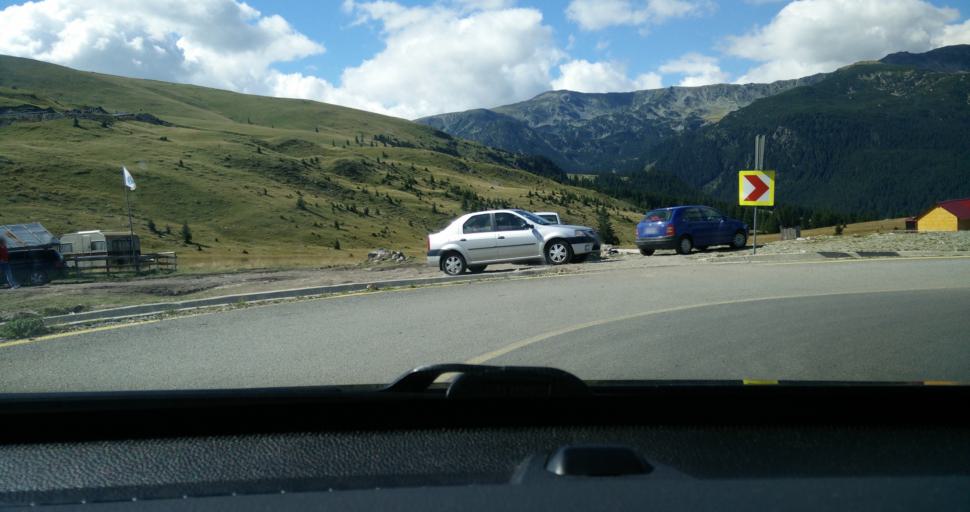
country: RO
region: Gorj
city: Novaci-Straini
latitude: 45.3853
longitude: 23.6417
